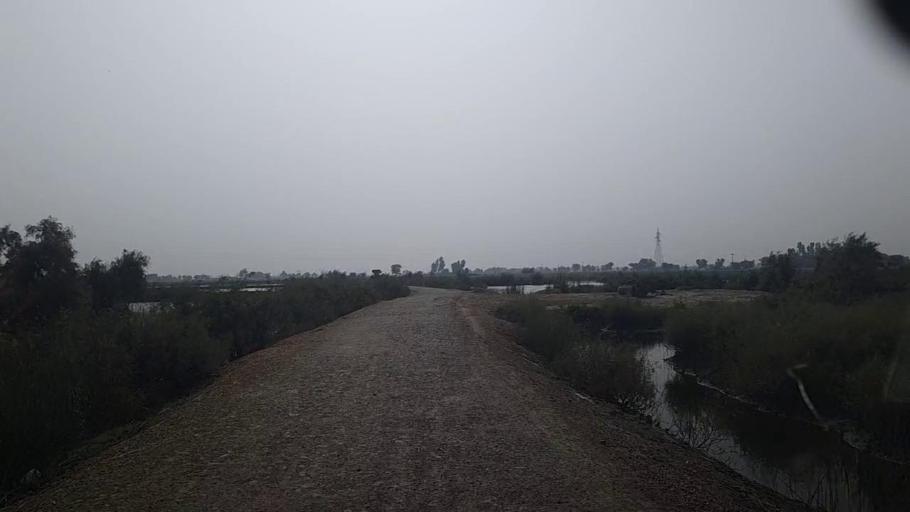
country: PK
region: Sindh
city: Kashmor
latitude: 28.3957
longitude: 69.4208
